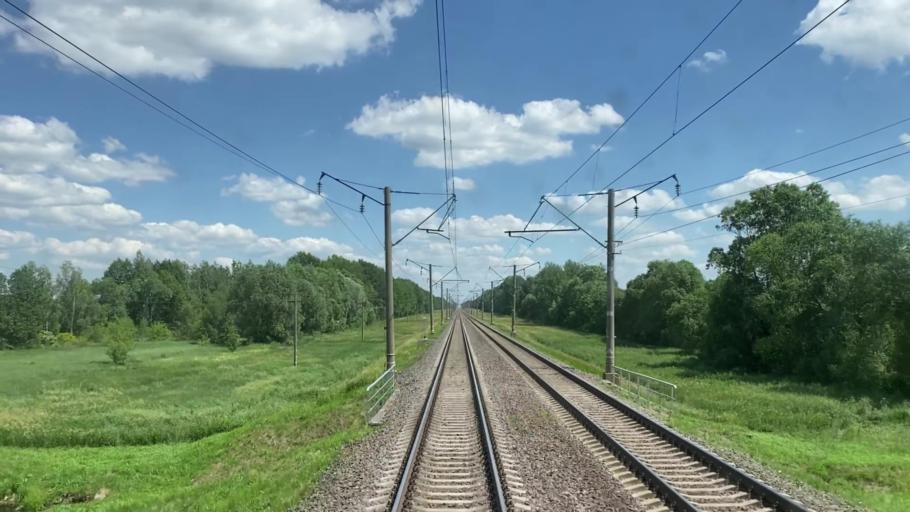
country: BY
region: Brest
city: Pruzhany
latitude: 52.5048
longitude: 24.6534
